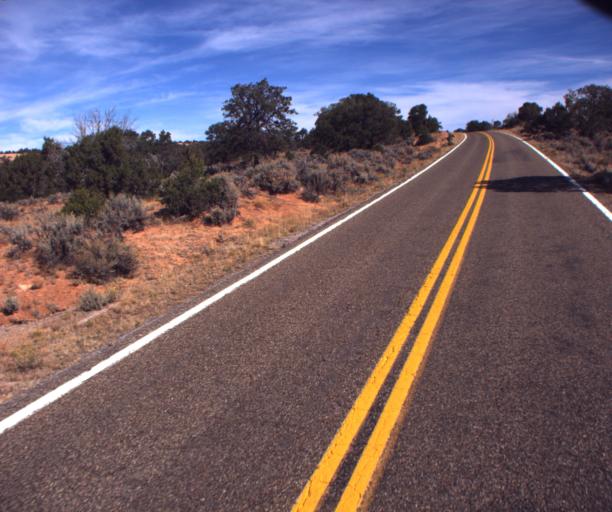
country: US
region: Arizona
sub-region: Navajo County
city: Kayenta
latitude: 36.5745
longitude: -110.4938
